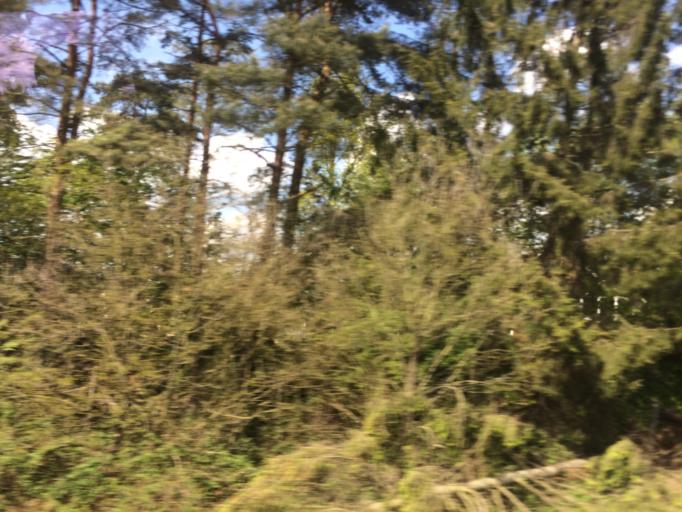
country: DE
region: Schleswig-Holstein
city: Brokstedt
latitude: 53.9919
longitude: 9.8273
